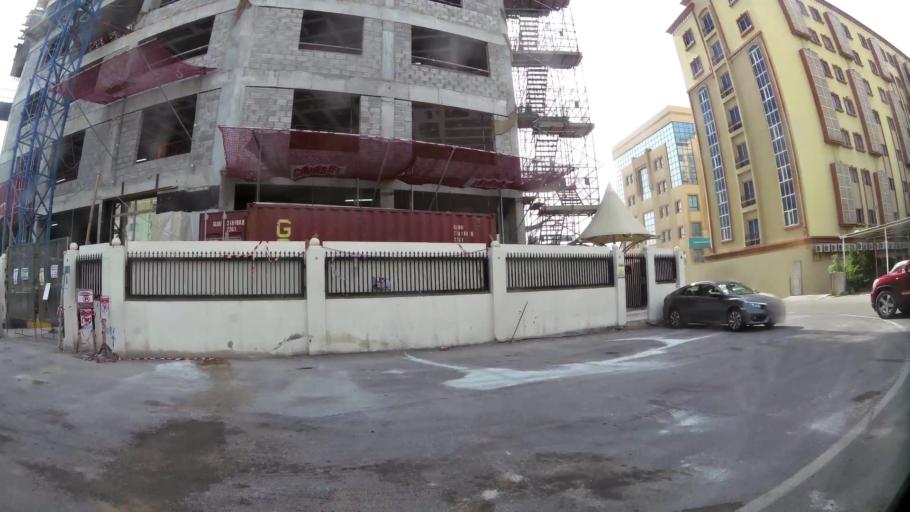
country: QA
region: Baladiyat ad Dawhah
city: Doha
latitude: 25.2752
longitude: 51.5101
